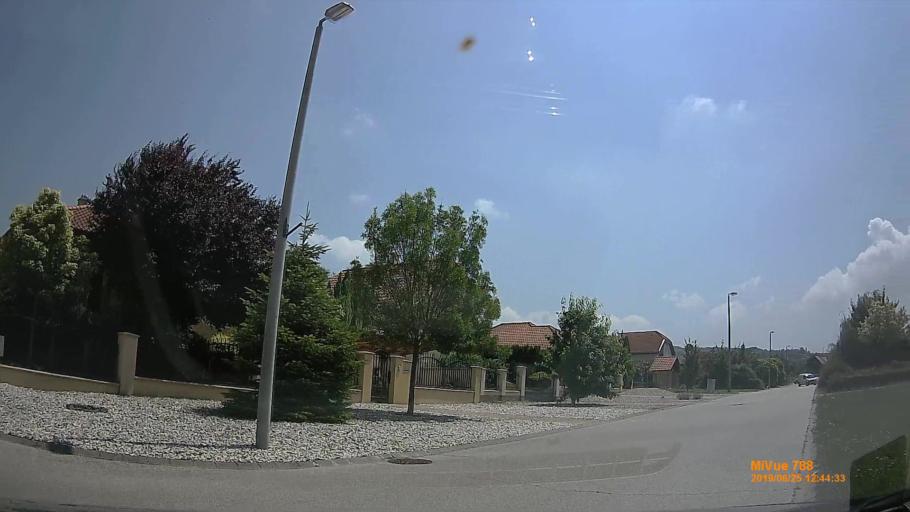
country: HU
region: Komarom-Esztergom
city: Esztergom
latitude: 47.8104
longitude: 18.7455
